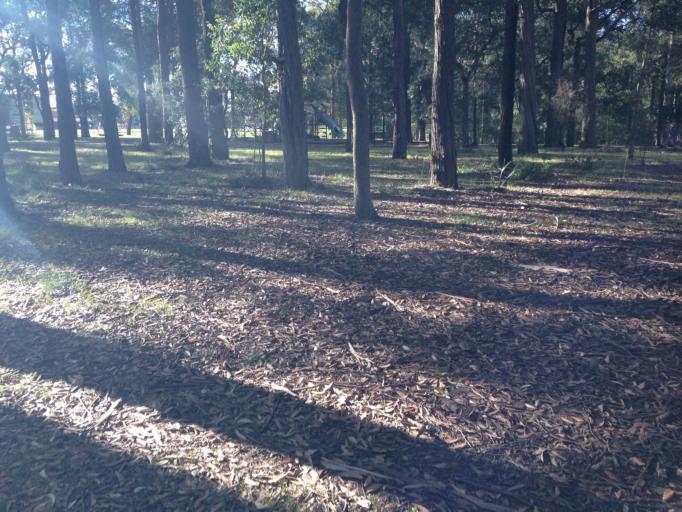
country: AU
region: New South Wales
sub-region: Ku-ring-gai
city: Killara
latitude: -33.7615
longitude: 151.1709
